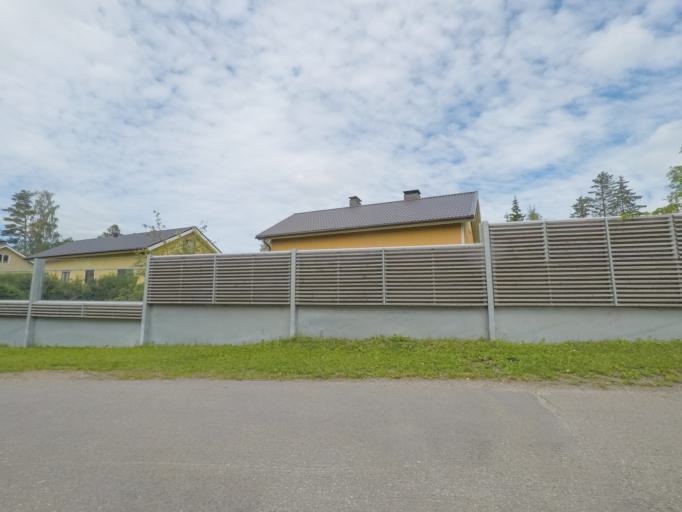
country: FI
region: Southern Savonia
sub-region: Savonlinna
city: Savonlinna
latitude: 61.8833
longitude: 28.8543
